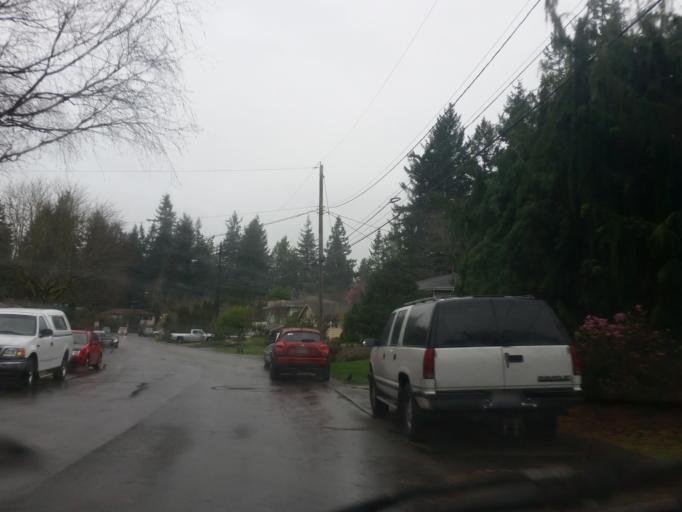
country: US
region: Washington
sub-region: Snohomish County
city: Lynnwood
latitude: 47.8197
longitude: -122.3461
